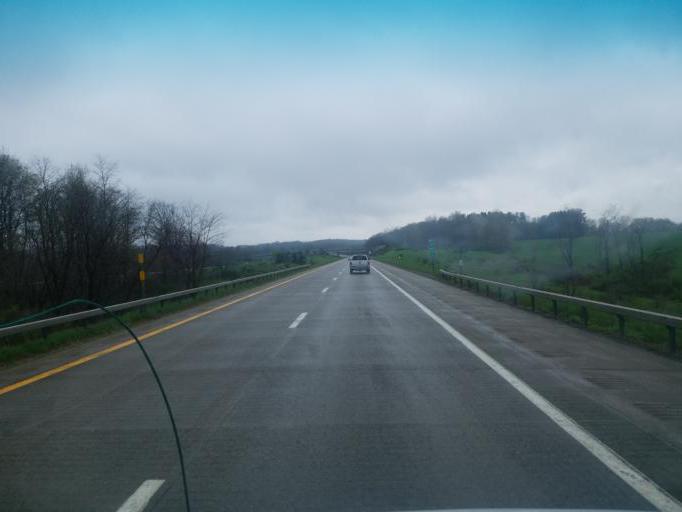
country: US
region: New York
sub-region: Chautauqua County
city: Clymer
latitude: 42.1480
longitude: -79.6468
